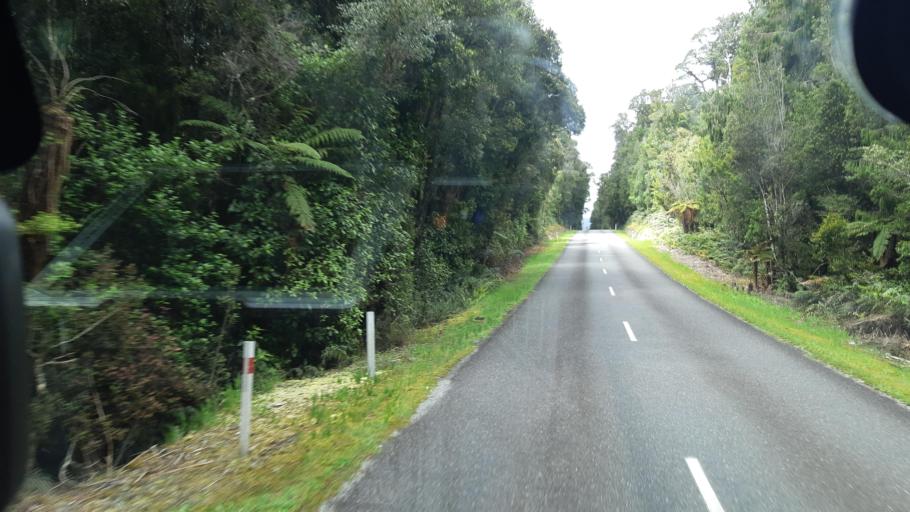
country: NZ
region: West Coast
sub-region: Westland District
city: Hokitika
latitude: -42.7807
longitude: 171.1075
